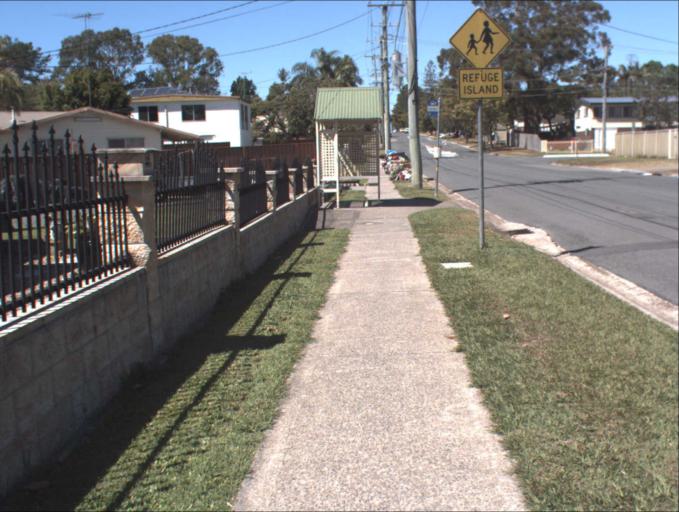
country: AU
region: Queensland
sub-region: Logan
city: Logan City
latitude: -27.6344
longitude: 153.1257
